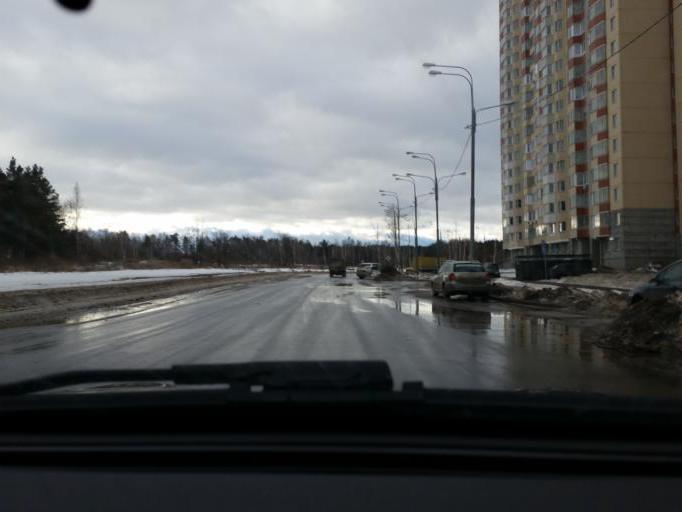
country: RU
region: Moskovskaya
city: Shcherbinka
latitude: 55.5221
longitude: 37.5986
